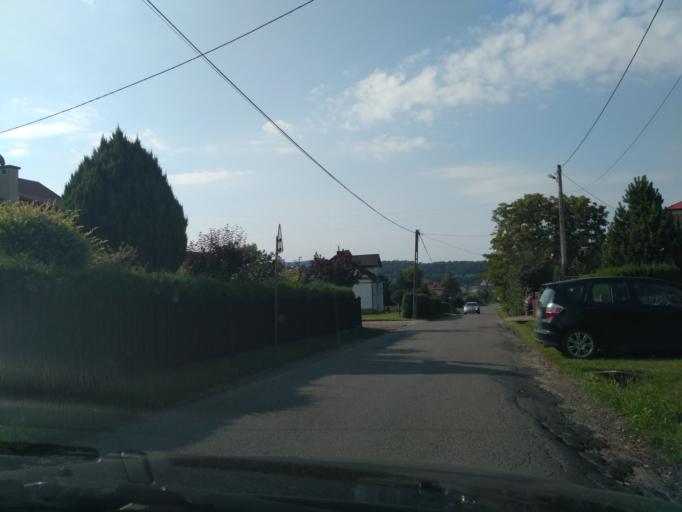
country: PL
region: Subcarpathian Voivodeship
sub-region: Powiat strzyzowski
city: Strzyzow
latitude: 49.8791
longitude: 21.7557
